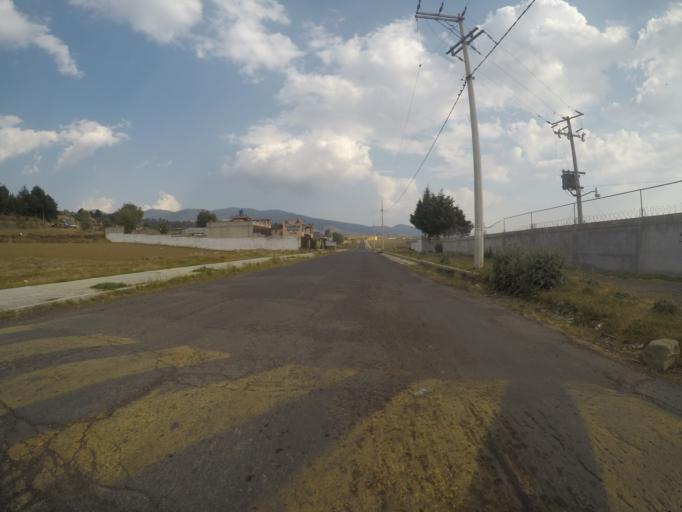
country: MX
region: Mexico
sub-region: Xalatlaco
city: El Aguila (La Mesa)
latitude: 19.1642
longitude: -99.4070
